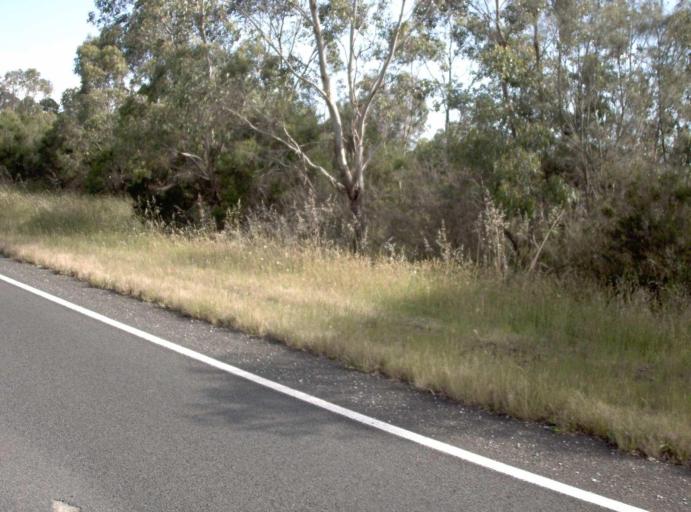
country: AU
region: Victoria
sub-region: Cardinia
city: Koo-Wee-Rup
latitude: -38.3230
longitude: 145.5421
